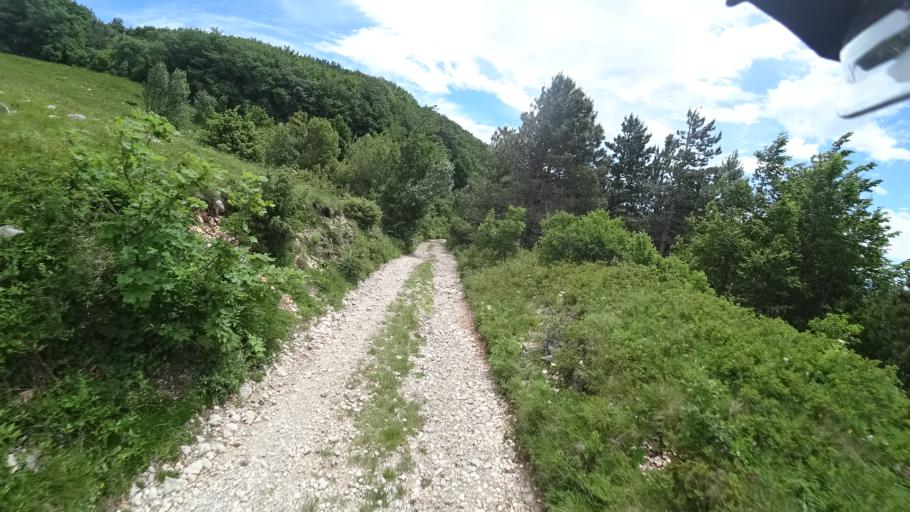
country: HR
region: Primorsko-Goranska
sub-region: Grad Crikvenica
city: Jadranovo
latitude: 45.2500
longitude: 14.6700
